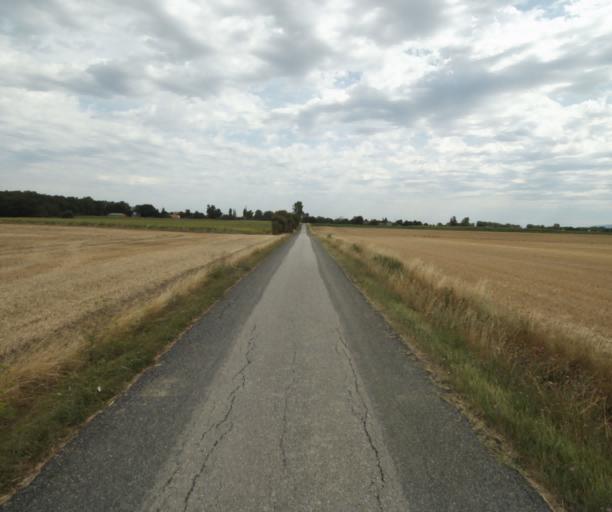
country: FR
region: Midi-Pyrenees
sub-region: Departement de la Haute-Garonne
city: Saint-Felix-Lauragais
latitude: 43.4427
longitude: 1.9287
